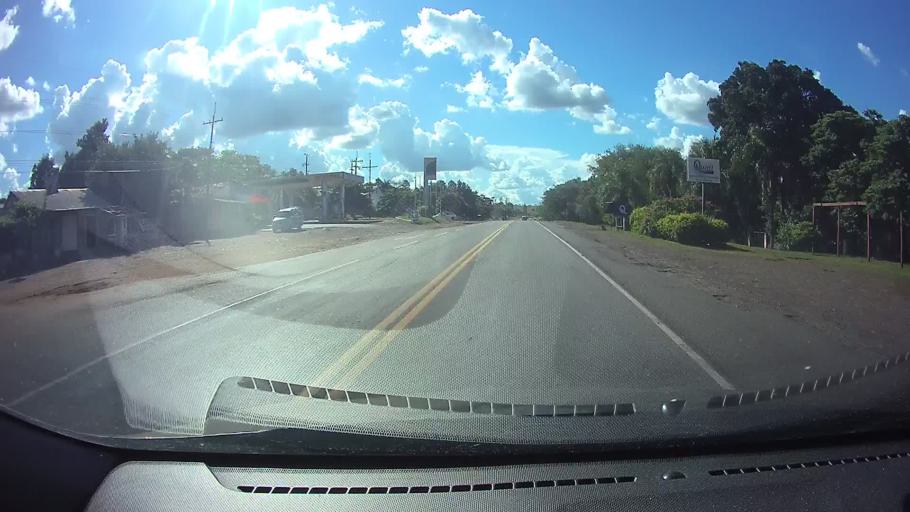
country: PY
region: Cordillera
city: Itacurubi de la Cordillera
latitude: -25.4552
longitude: -56.8957
